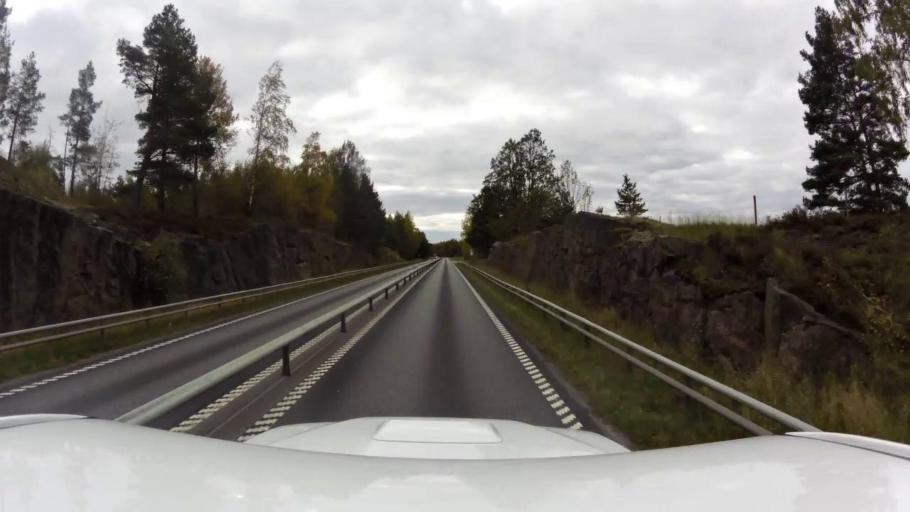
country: SE
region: OEstergoetland
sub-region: Linkopings Kommun
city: Malmslatt
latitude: 58.2979
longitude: 15.5641
